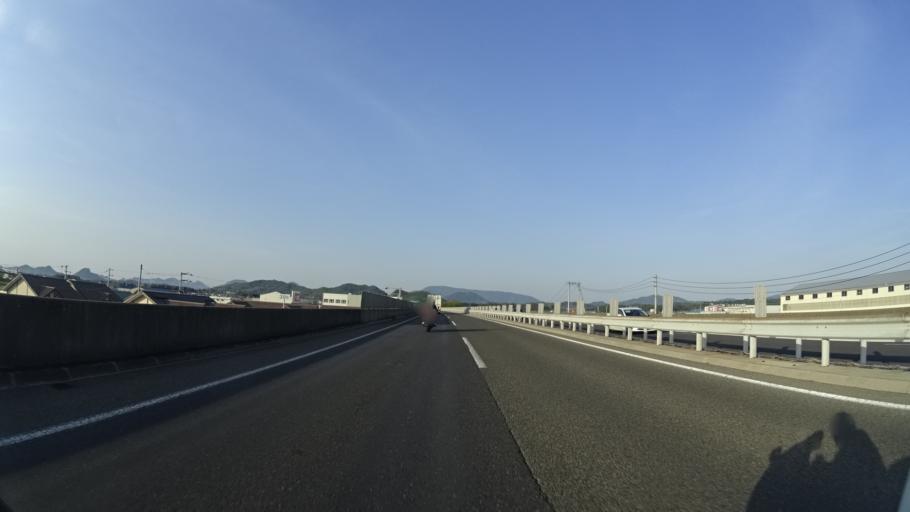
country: JP
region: Kagawa
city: Kan'onjicho
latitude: 34.1308
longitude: 133.7038
